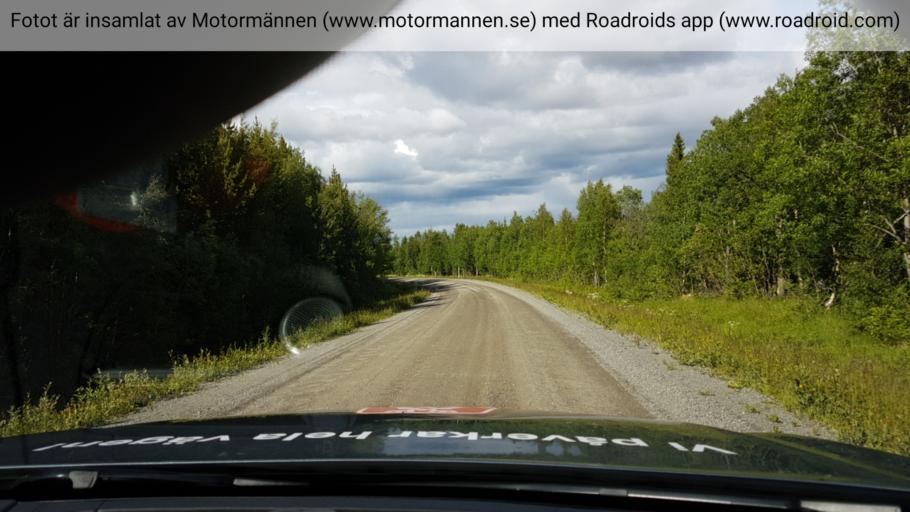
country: SE
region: Jaemtland
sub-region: Krokoms Kommun
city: Valla
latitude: 63.0504
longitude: 13.9629
